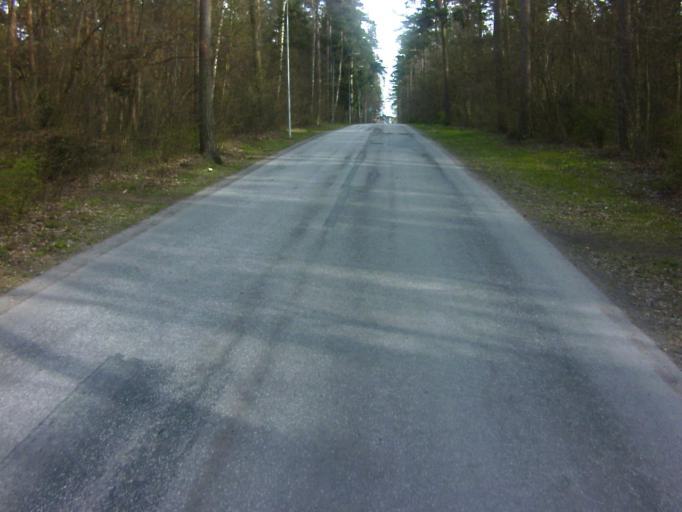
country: SE
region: Skane
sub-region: Kavlinge Kommun
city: Kaevlinge
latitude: 55.7784
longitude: 13.0917
